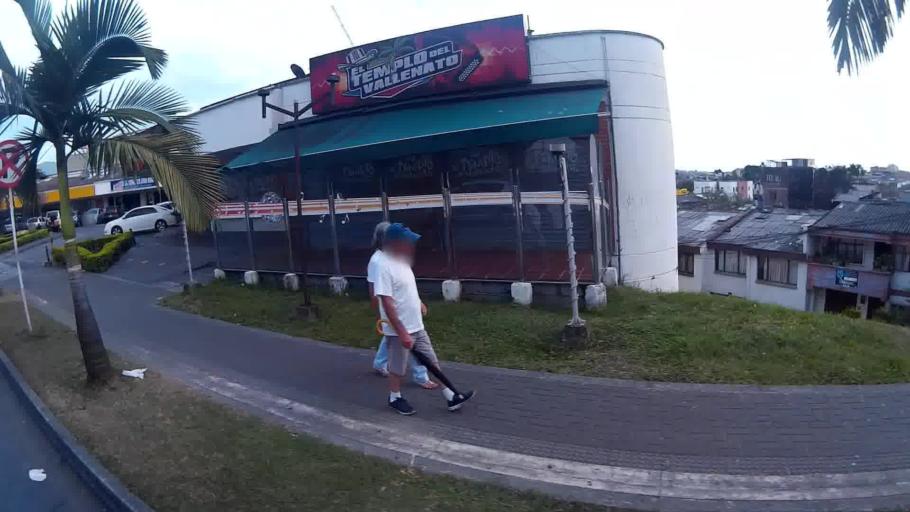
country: CO
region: Risaralda
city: Pereira
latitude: 4.8097
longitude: -75.6980
